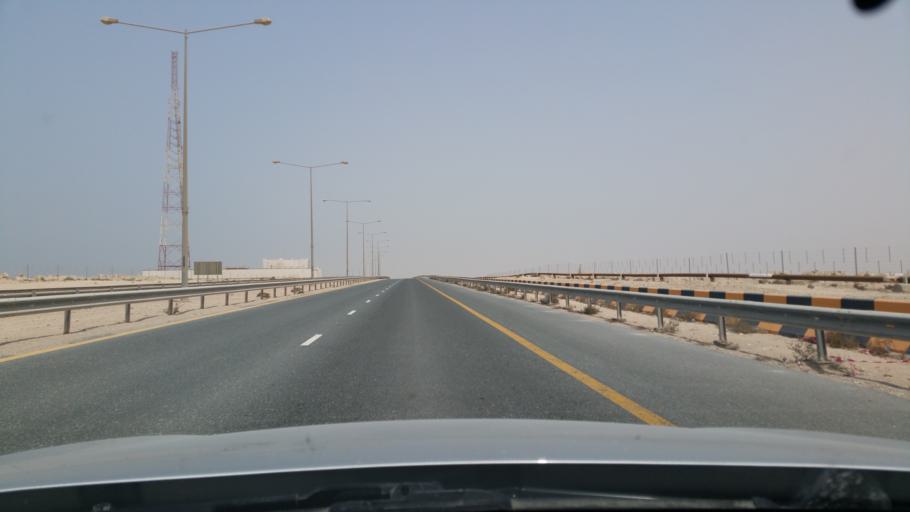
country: QA
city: Umm Bab
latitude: 25.3089
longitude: 50.7921
